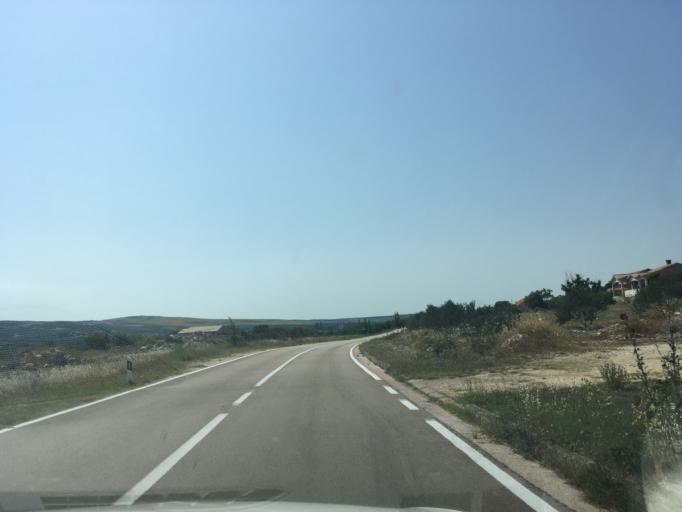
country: HR
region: Zadarska
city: Benkovac
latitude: 43.9652
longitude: 15.7299
